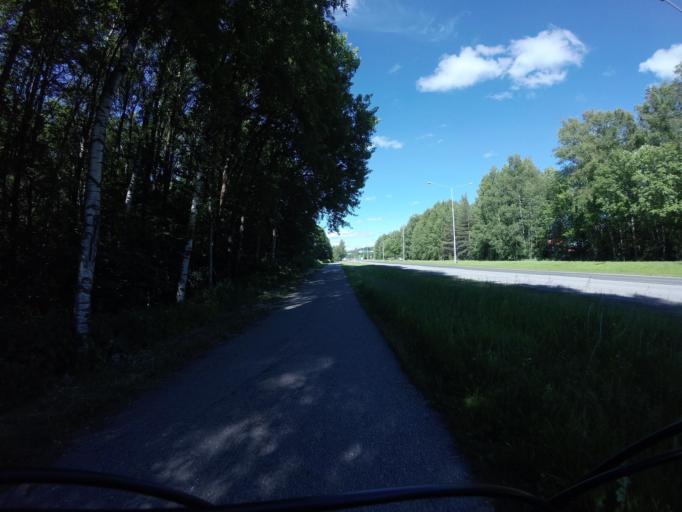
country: FI
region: Varsinais-Suomi
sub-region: Turku
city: Turku
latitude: 60.4882
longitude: 22.2775
